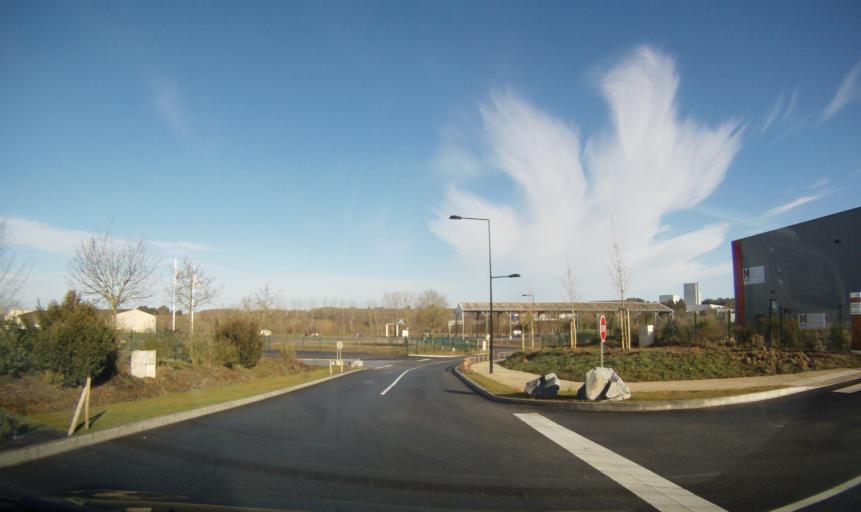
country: FR
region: Brittany
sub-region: Departement d'Ille-et-Vilaine
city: Crevin
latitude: 47.9339
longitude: -1.6706
